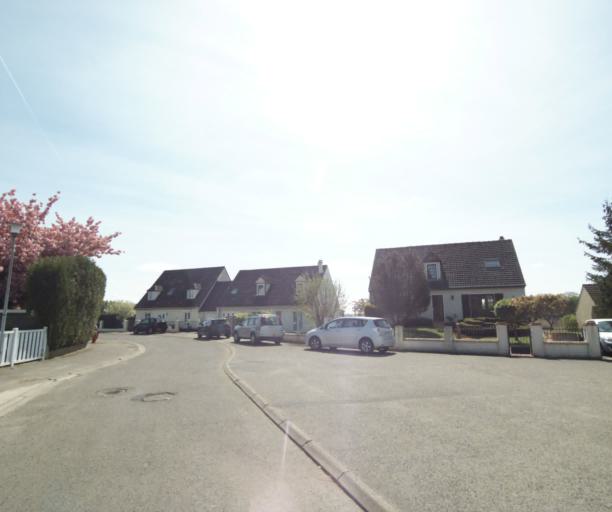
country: FR
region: Ile-de-France
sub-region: Departement de Seine-et-Marne
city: Nangis
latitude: 48.5495
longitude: 3.0128
